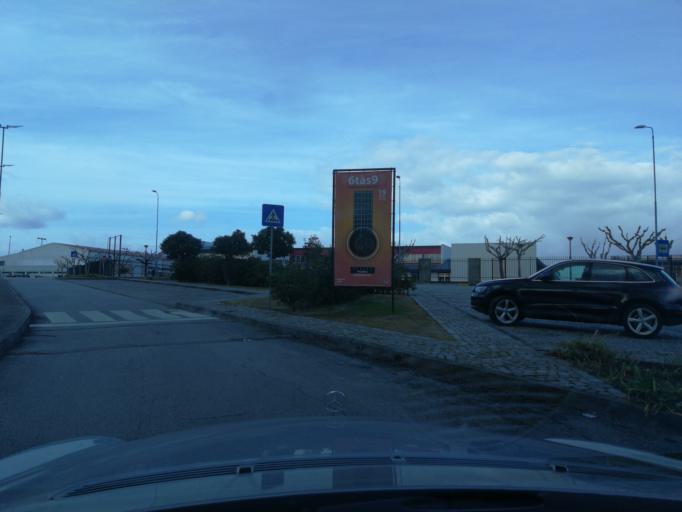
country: PT
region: Viana do Castelo
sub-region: Valenca
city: Valenza
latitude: 42.0284
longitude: -8.6385
